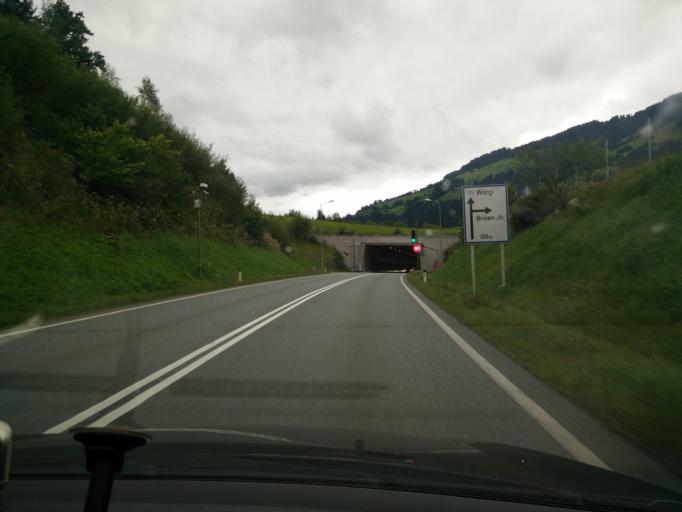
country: AT
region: Tyrol
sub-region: Politischer Bezirk Kitzbuhel
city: Brixen im Thale
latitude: 47.4451
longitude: 12.2446
